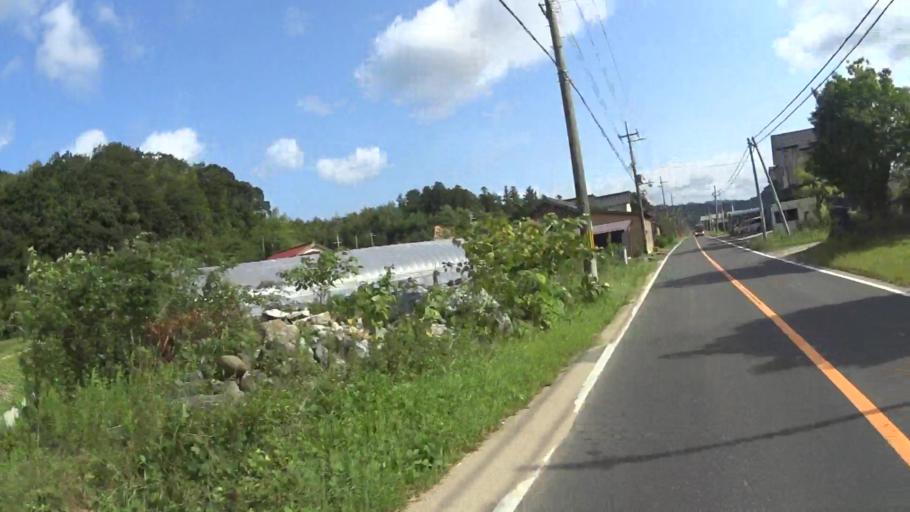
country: JP
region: Kyoto
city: Miyazu
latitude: 35.5968
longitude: 135.0956
